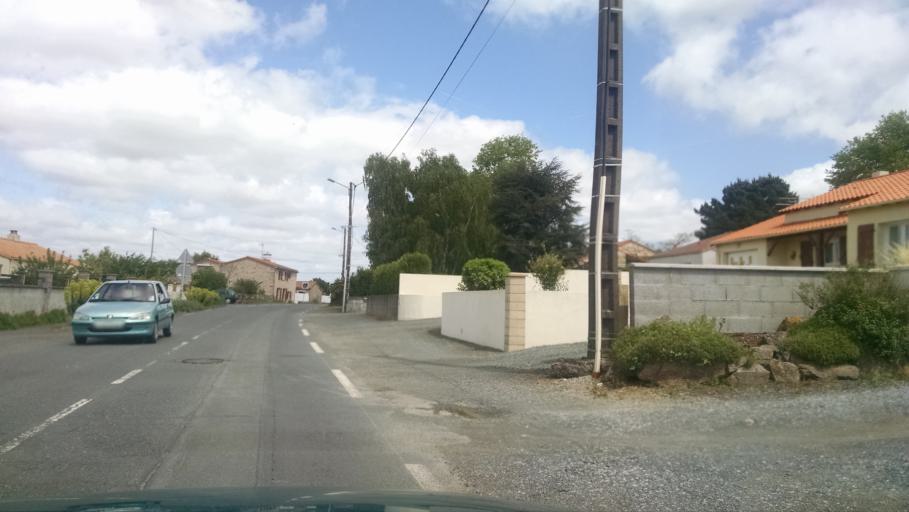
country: FR
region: Pays de la Loire
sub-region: Departement de la Loire-Atlantique
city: Gorges
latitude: 47.0954
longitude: -1.3098
